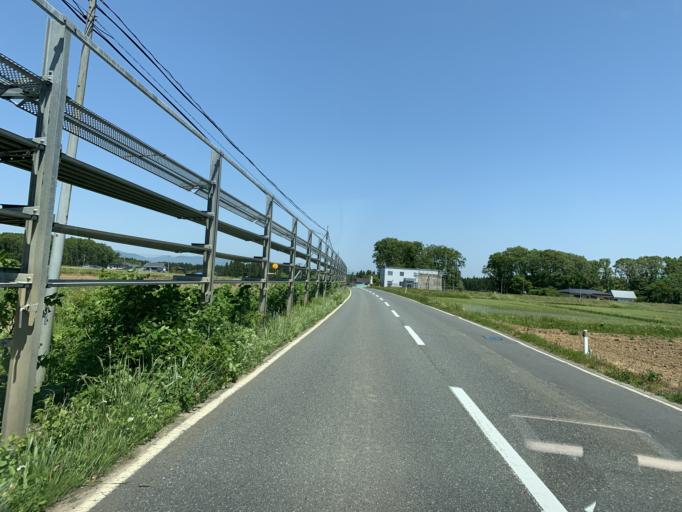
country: JP
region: Iwate
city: Kitakami
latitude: 39.2585
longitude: 141.0643
